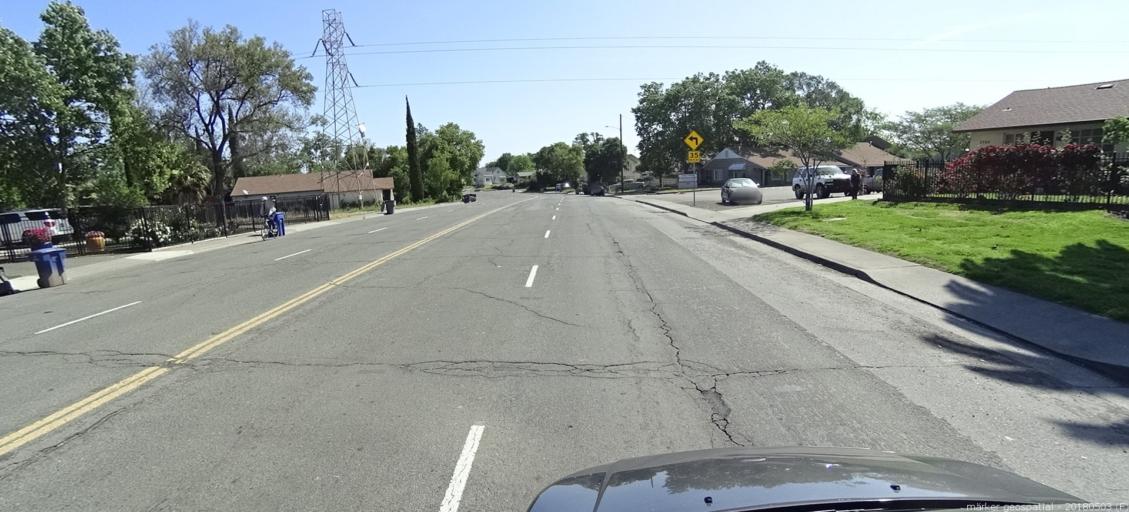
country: US
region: California
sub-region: Sacramento County
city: Arden-Arcade
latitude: 38.6199
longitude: -121.4345
